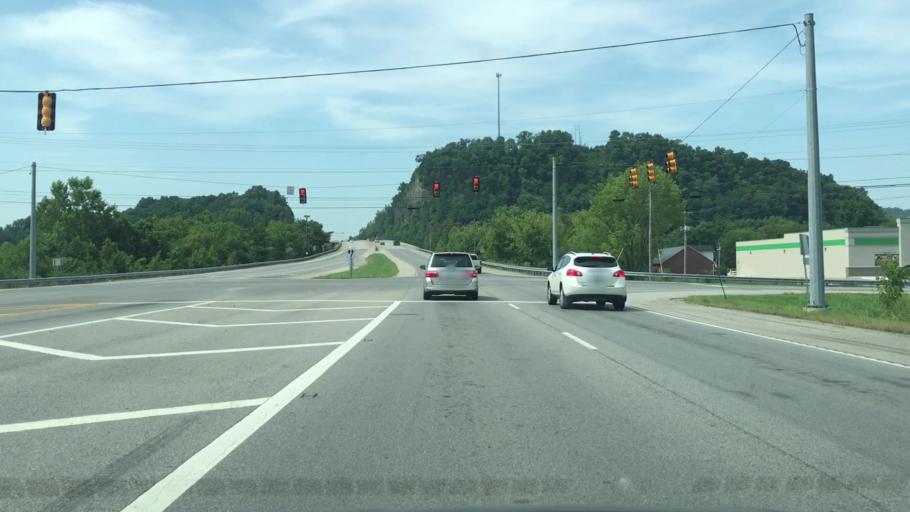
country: US
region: Tennessee
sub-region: Smith County
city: South Carthage
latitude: 36.2448
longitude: -85.9420
